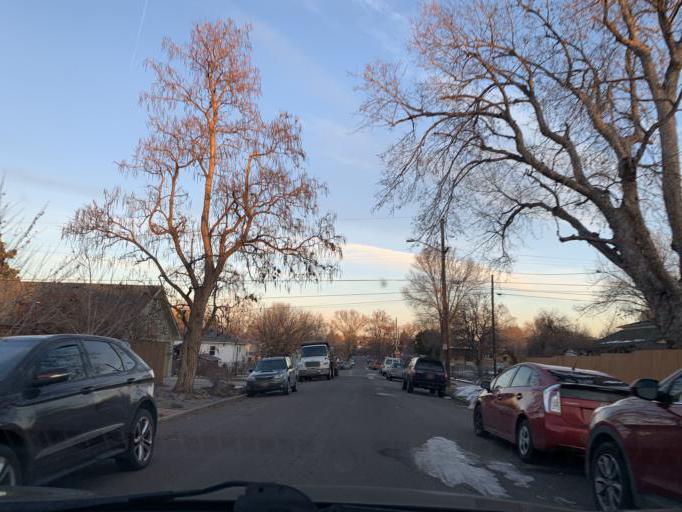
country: US
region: Colorado
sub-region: Adams County
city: Berkley
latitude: 39.7892
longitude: -105.0380
